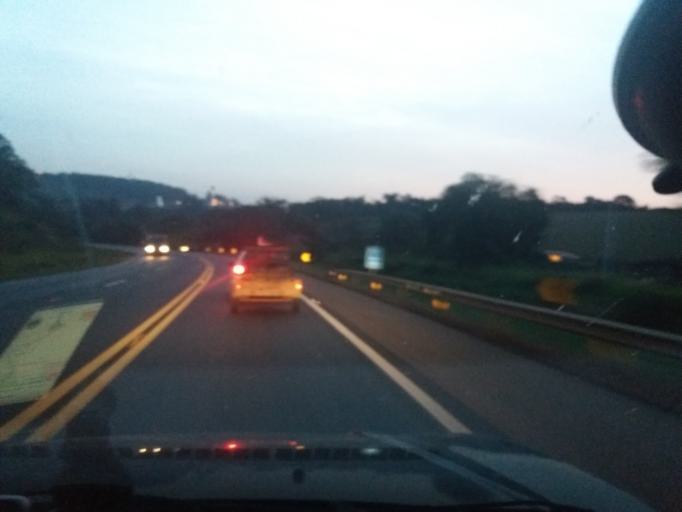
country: BR
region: Sao Paulo
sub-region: Itapeva
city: Itapeva
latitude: -23.9759
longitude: -48.8405
